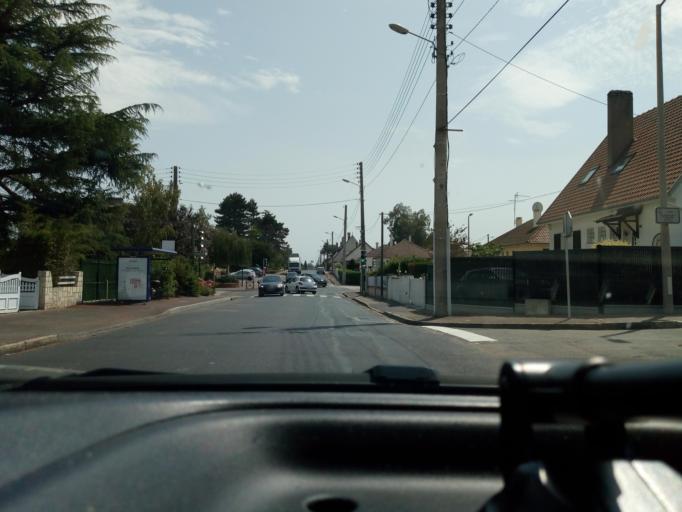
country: FR
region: Haute-Normandie
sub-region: Departement de la Seine-Maritime
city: Le Petit-Quevilly
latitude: 49.4041
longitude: 1.0580
